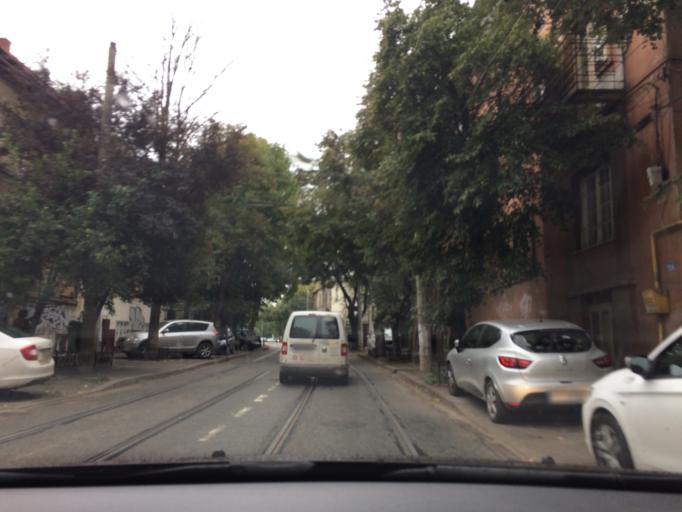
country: RO
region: Timis
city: Timisoara
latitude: 45.7559
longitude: 21.2212
